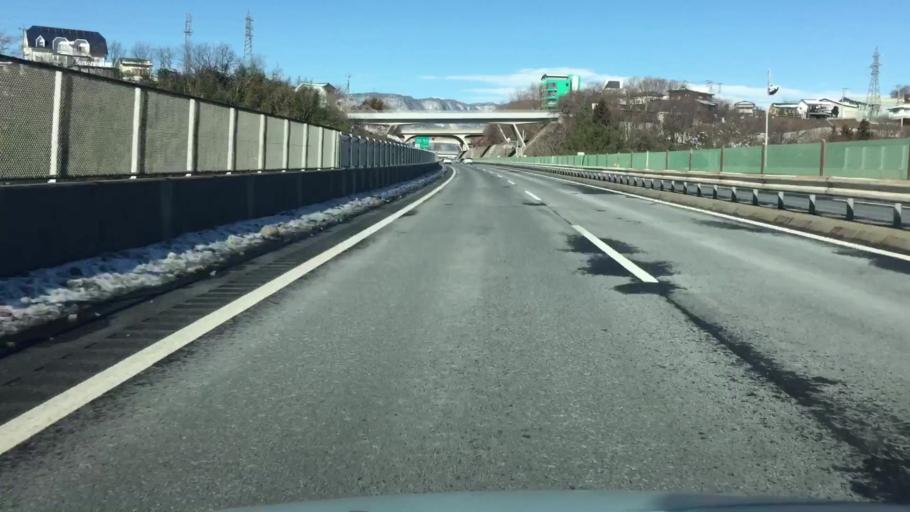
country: JP
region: Gunma
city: Numata
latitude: 36.6512
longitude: 139.0756
